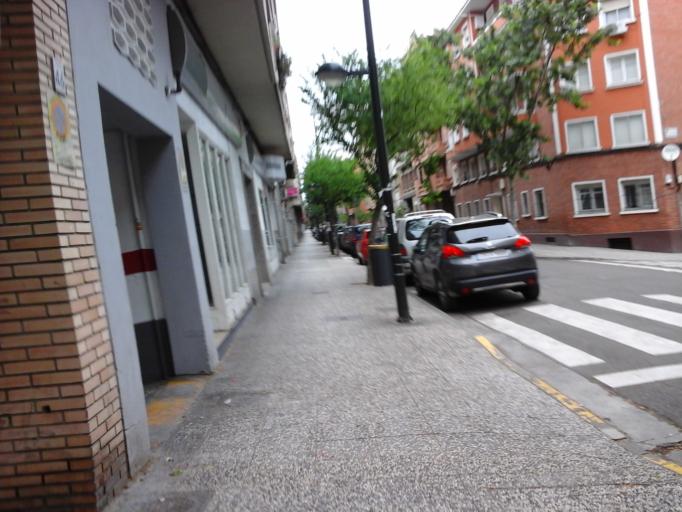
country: ES
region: Aragon
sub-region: Provincia de Zaragoza
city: Zaragoza
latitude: 41.6349
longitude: -0.8816
